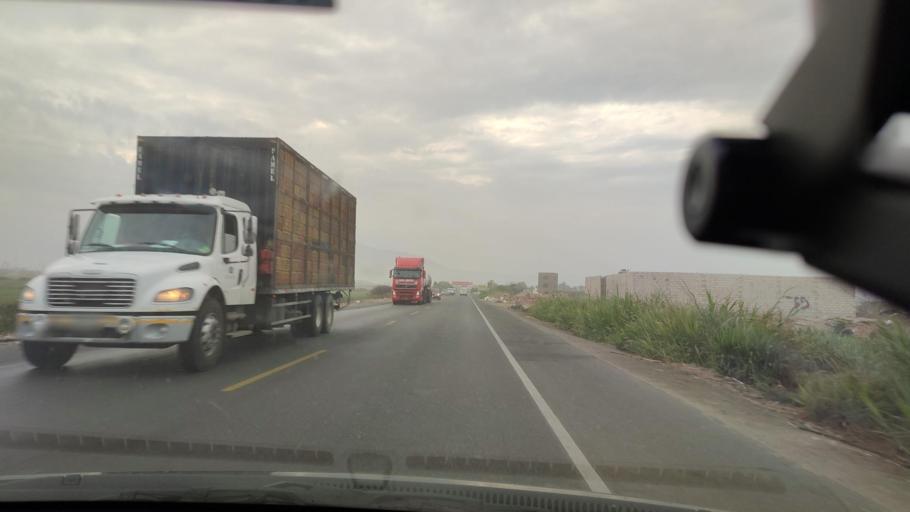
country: PE
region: La Libertad
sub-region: Provincia de Trujillo
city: Buenos Aires
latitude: -8.1325
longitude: -79.0665
